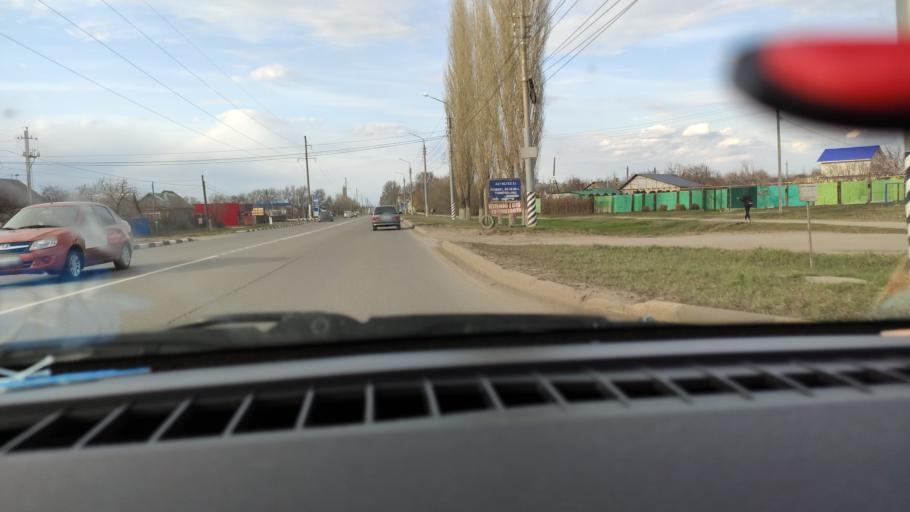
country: RU
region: Saratov
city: Privolzhskiy
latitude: 51.4023
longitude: 46.0371
